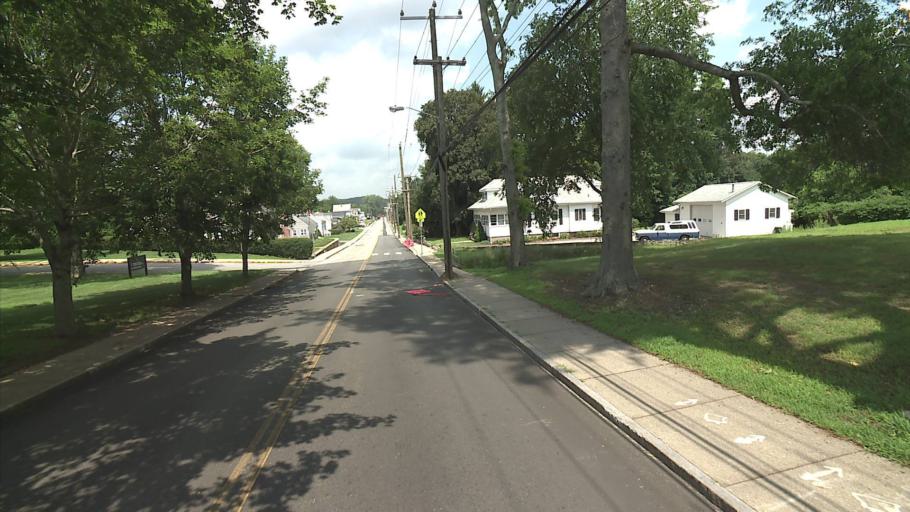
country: US
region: Connecticut
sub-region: New London County
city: Jewett City
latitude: 41.5980
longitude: -71.9791
